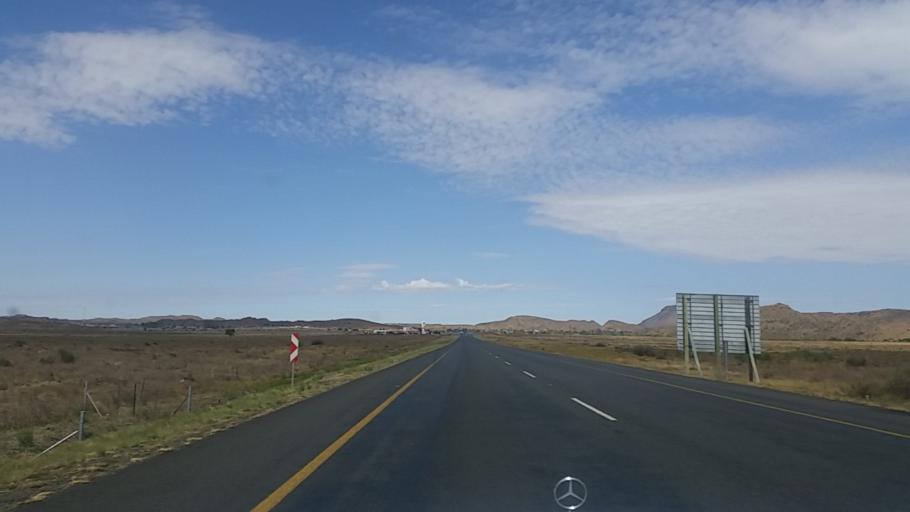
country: ZA
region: Northern Cape
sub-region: Pixley ka Seme District Municipality
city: Colesberg
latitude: -30.6960
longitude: 25.1353
